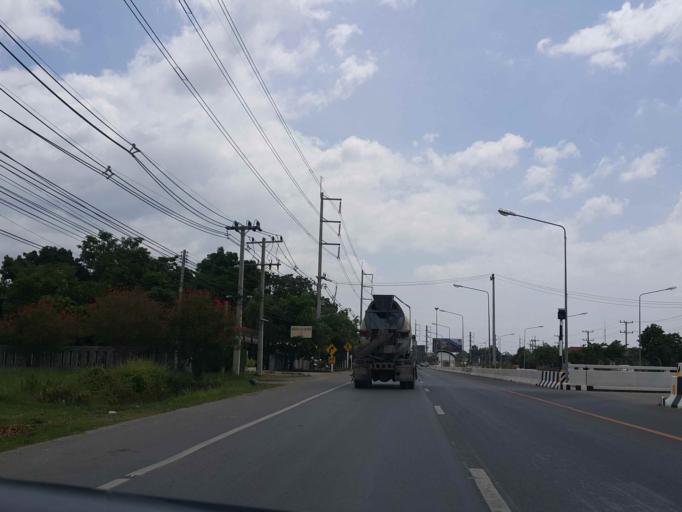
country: TH
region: Chiang Mai
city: Hang Dong
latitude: 18.7361
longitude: 98.9309
